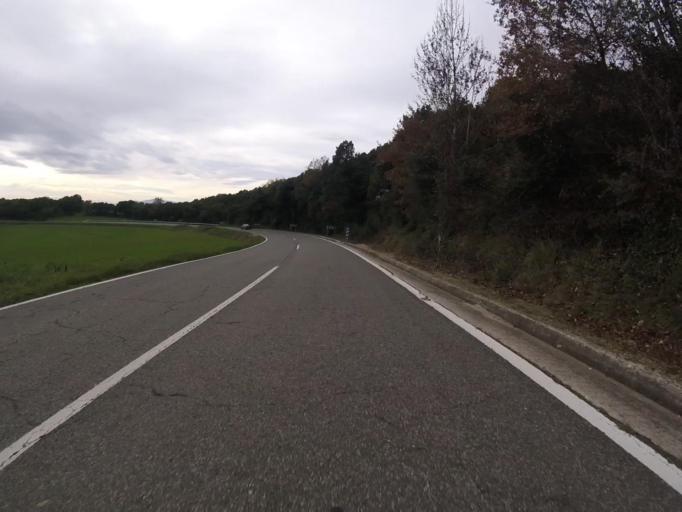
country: ES
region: Navarre
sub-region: Provincia de Navarra
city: Lezaun
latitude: 42.7536
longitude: -2.0176
